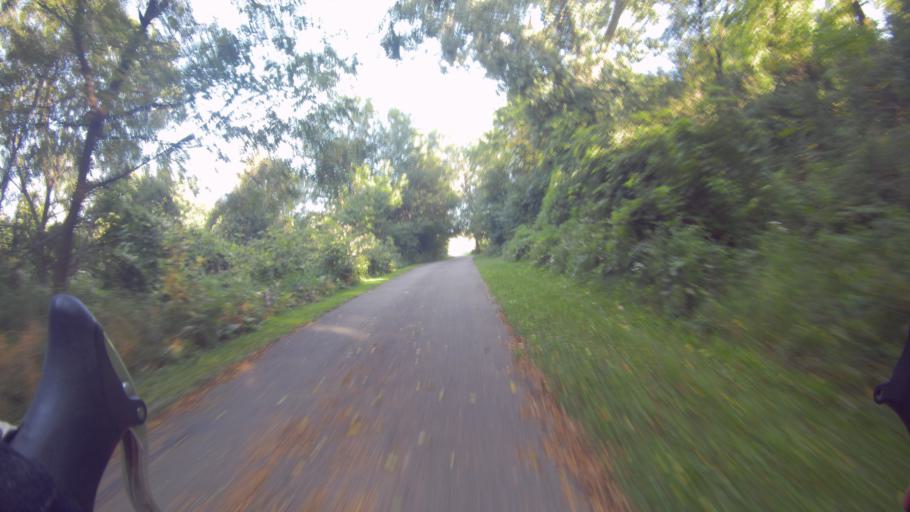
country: US
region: Wisconsin
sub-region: Dane County
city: Monona
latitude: 43.0324
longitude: -89.3504
